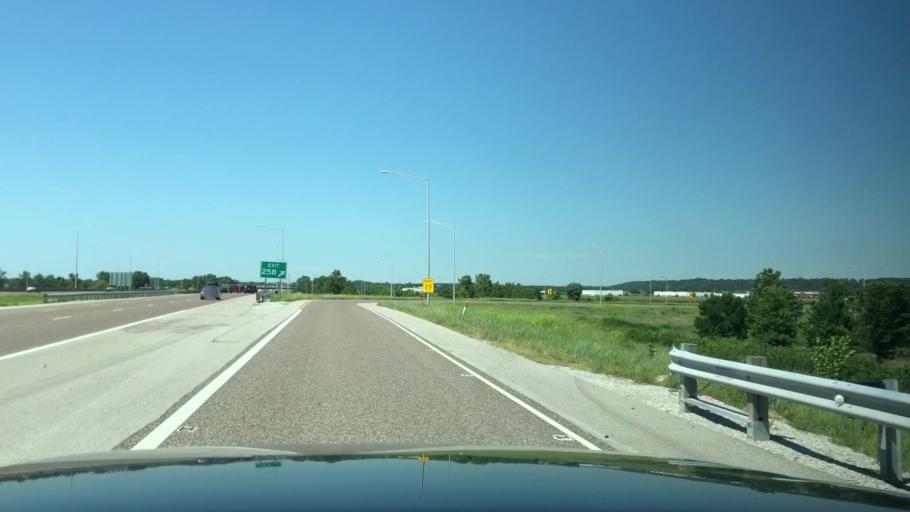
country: US
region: Illinois
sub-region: Saint Clair County
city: Caseyville
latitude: 38.6739
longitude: -90.0294
